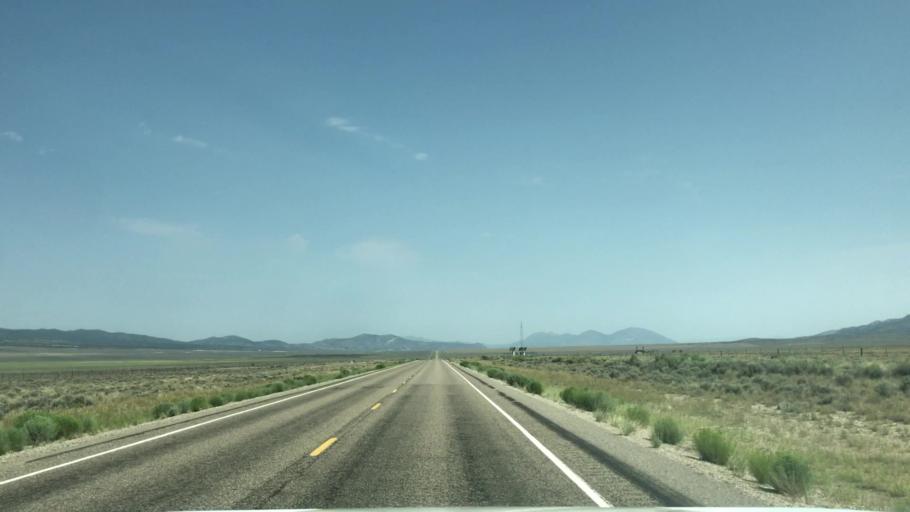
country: US
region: Nevada
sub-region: White Pine County
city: Ely
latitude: 39.0978
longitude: -114.7584
